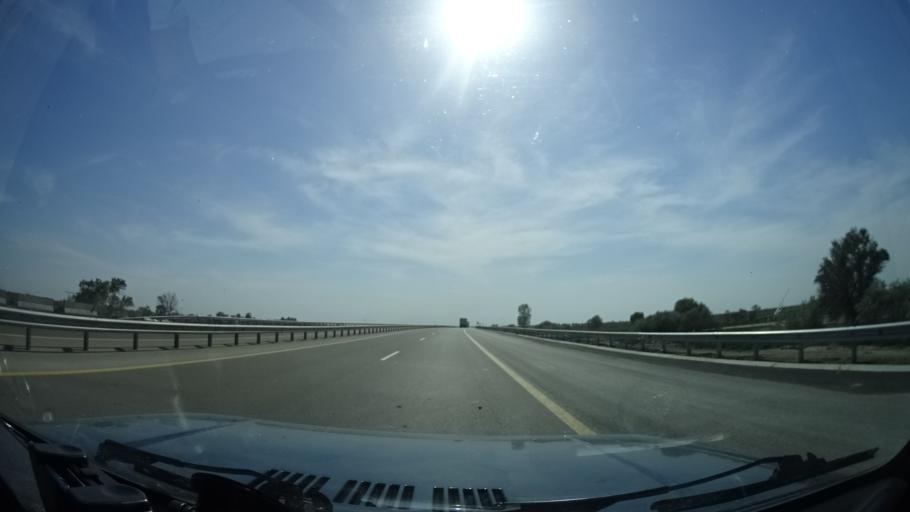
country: AZ
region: Salyan
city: Qaracala
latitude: 39.7412
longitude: 49.1249
